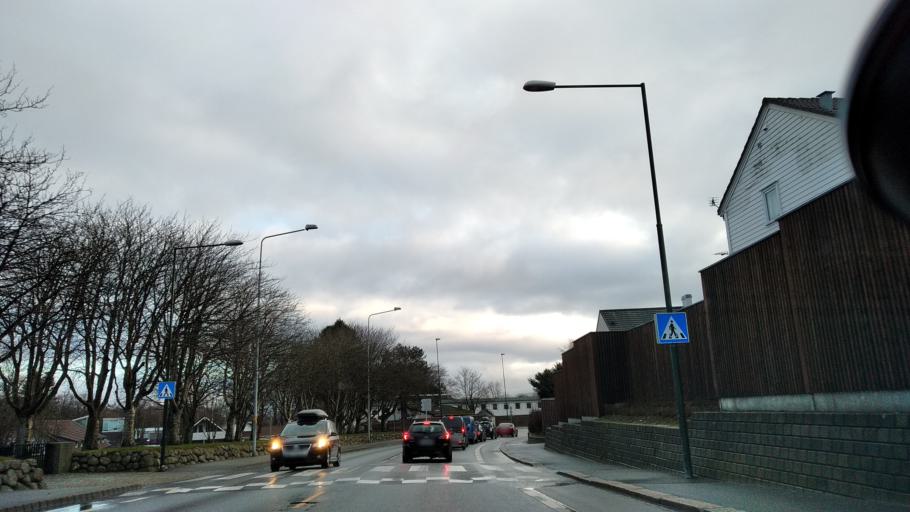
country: NO
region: Rogaland
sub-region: Stavanger
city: Stavanger
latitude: 58.9527
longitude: 5.7095
